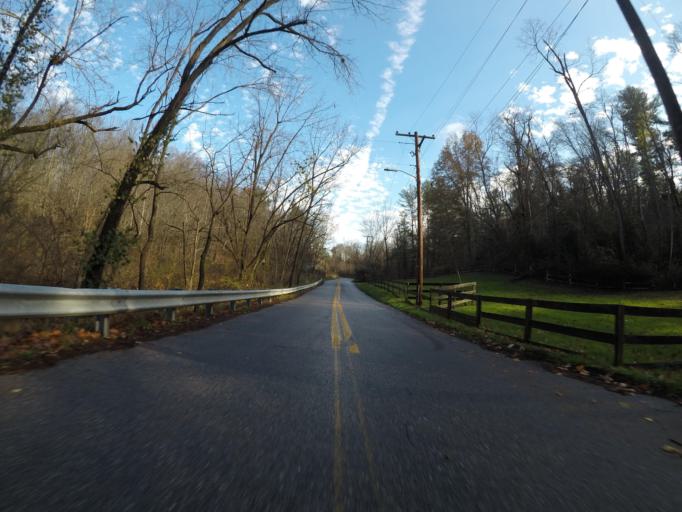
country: US
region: Maryland
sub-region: Carroll County
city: Hampstead
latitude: 39.5761
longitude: -76.8115
